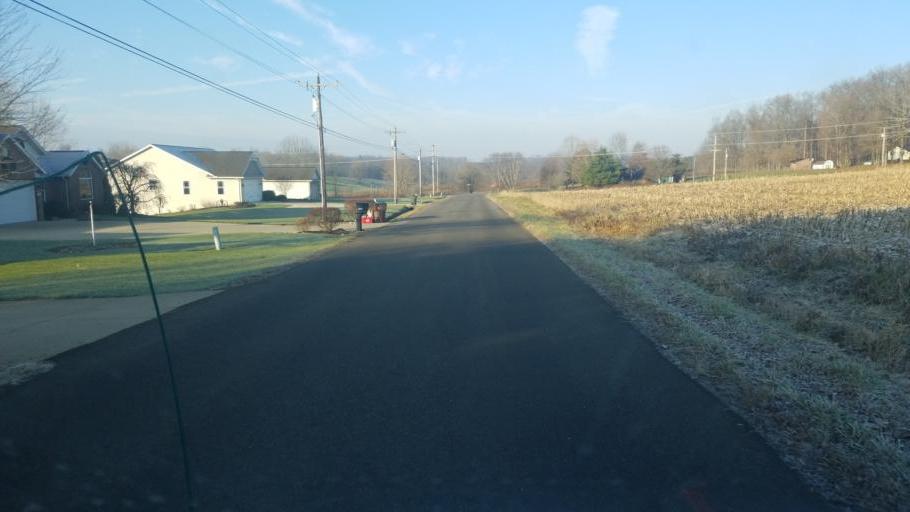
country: US
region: Ohio
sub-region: Knox County
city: Gambier
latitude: 40.4516
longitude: -82.3639
